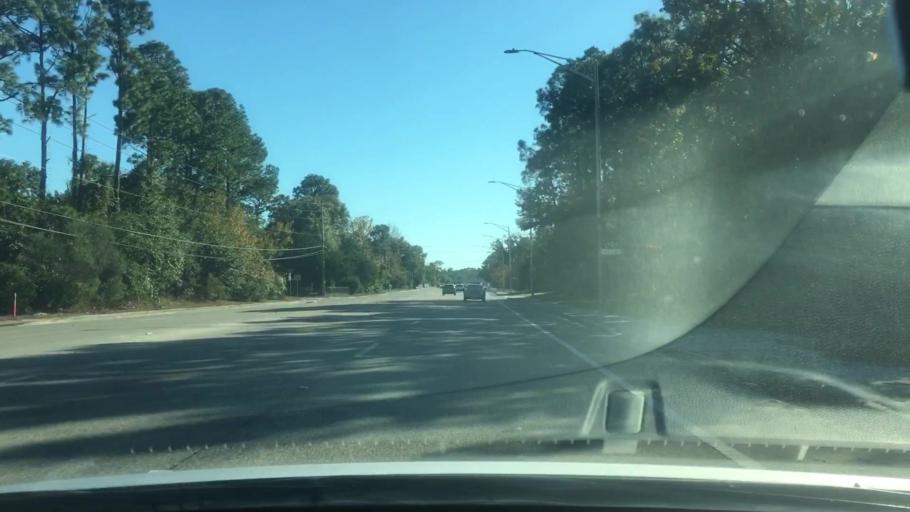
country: US
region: Florida
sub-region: Duval County
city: Neptune Beach
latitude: 30.2942
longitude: -81.4591
